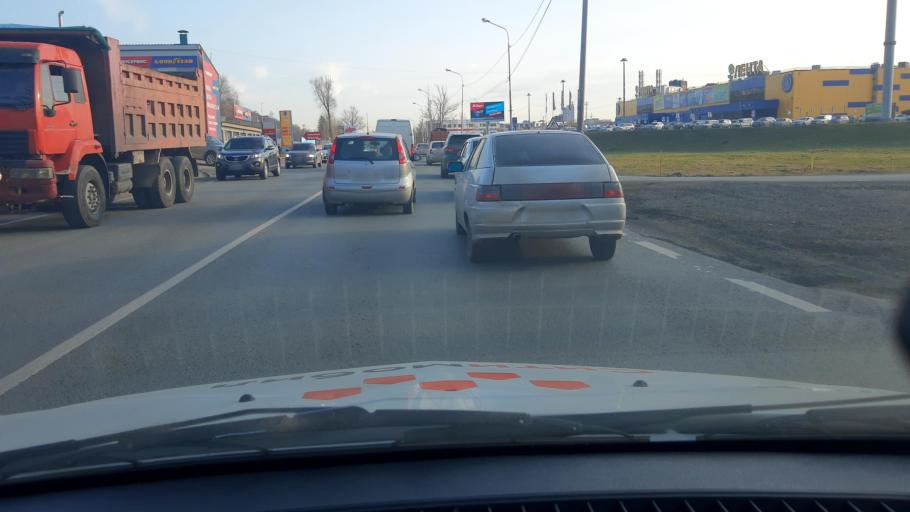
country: RU
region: Bashkortostan
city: Ufa
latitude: 54.6985
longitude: 55.9706
